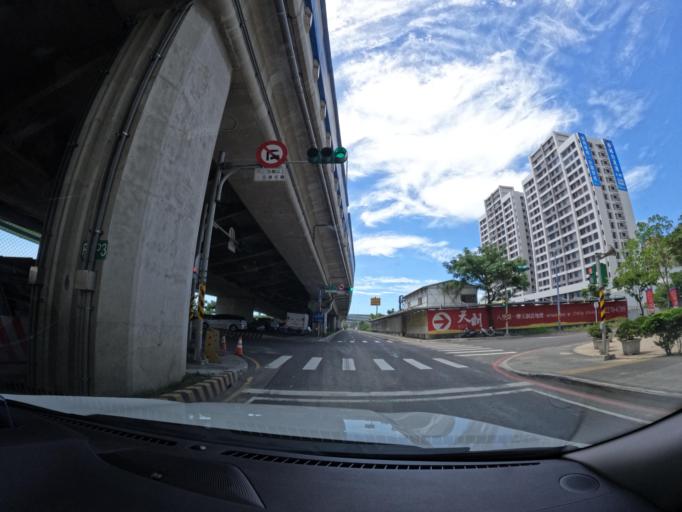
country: TW
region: Taipei
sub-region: Taipei
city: Banqiao
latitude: 25.1466
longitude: 121.3952
